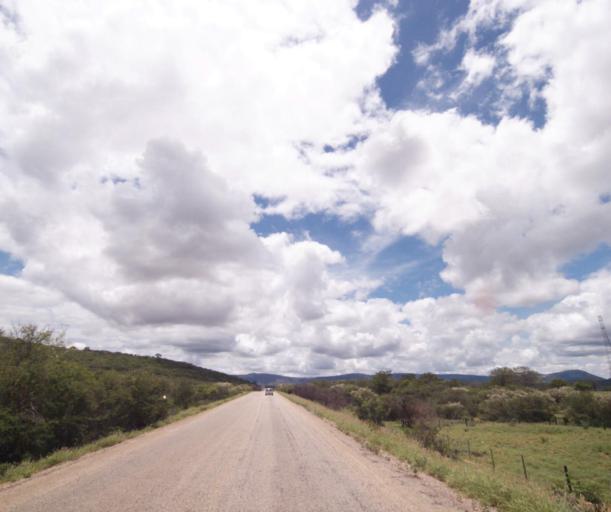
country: BR
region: Bahia
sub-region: Brumado
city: Brumado
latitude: -14.1999
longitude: -41.6071
